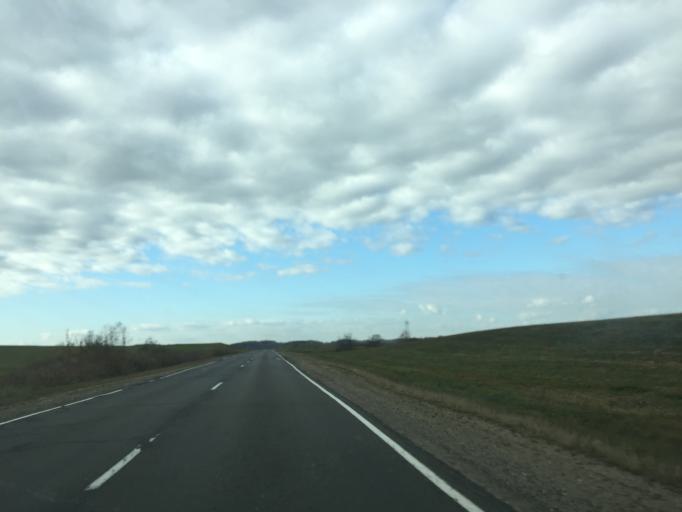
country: BY
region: Vitebsk
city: Mosar
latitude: 55.0623
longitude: 27.2557
